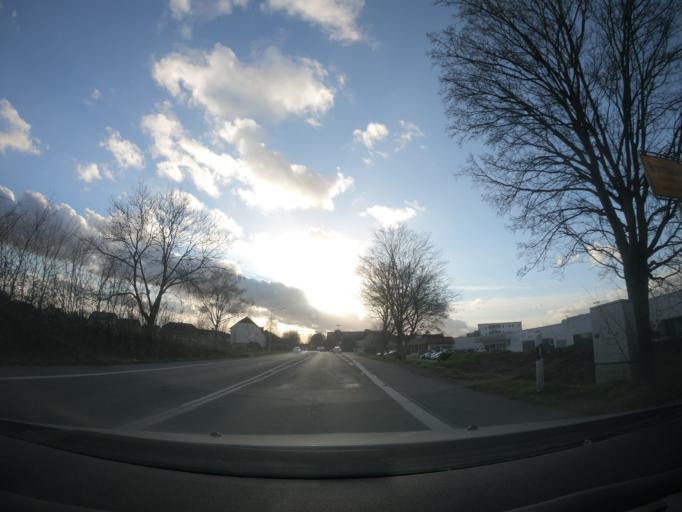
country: DE
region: North Rhine-Westphalia
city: Waltrop
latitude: 51.6027
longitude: 7.4595
